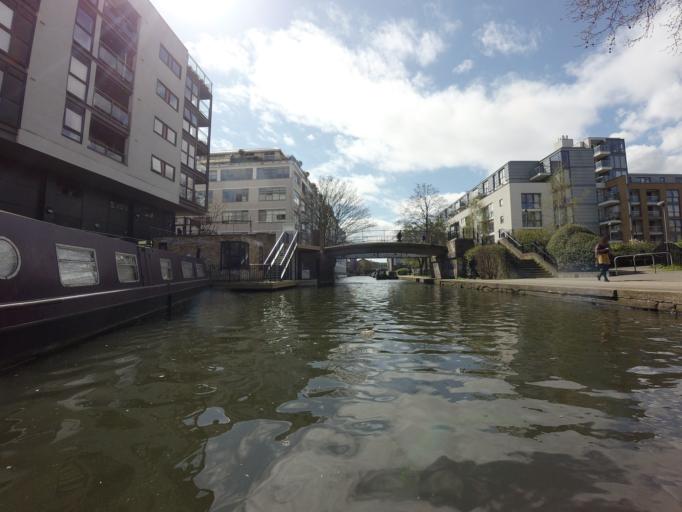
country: GB
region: England
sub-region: Greater London
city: Islington
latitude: 51.5336
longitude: -0.0944
